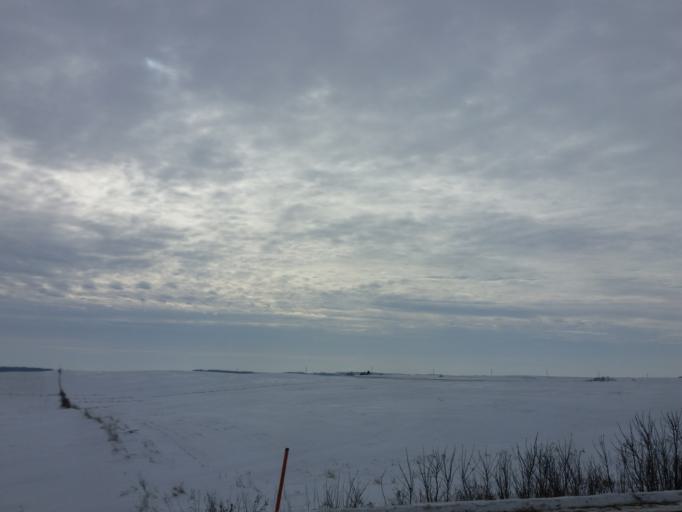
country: US
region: Iowa
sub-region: Dubuque County
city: Peosta
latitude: 42.3821
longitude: -90.7532
